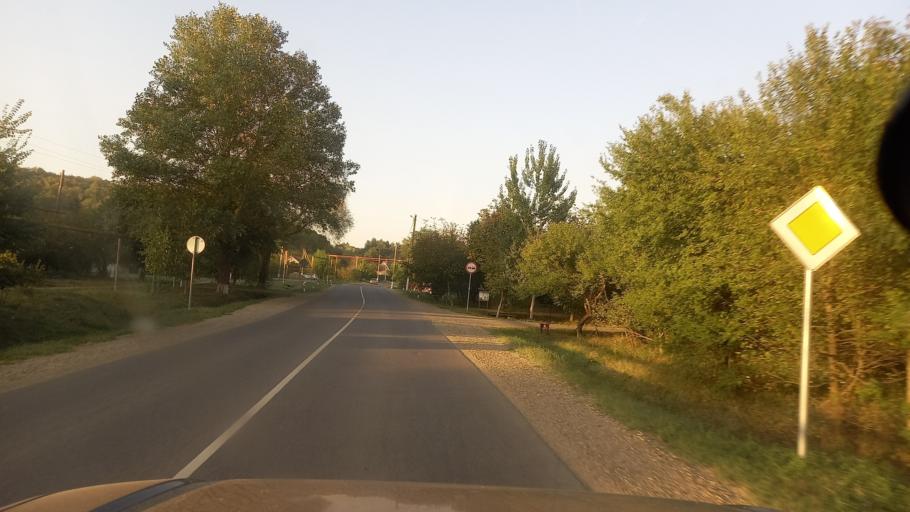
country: RU
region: Krasnodarskiy
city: Smolenskaya
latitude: 44.7667
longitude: 38.7789
